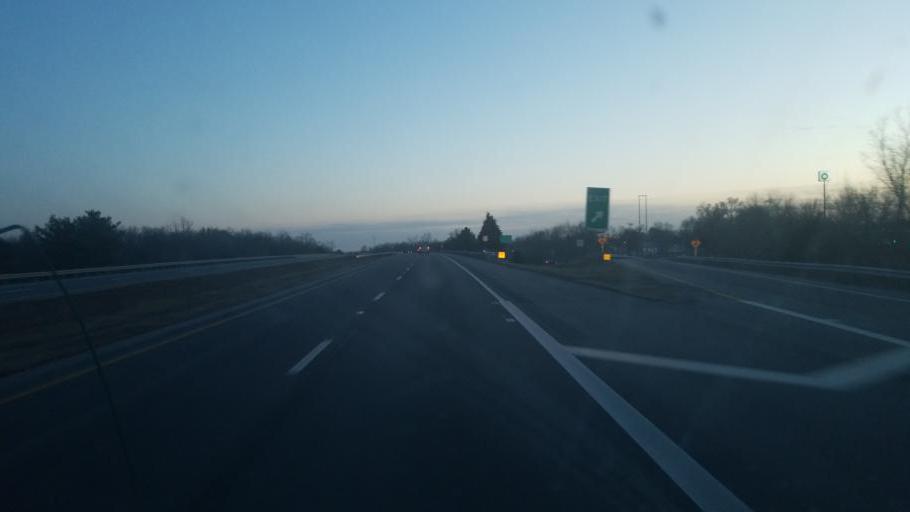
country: US
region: Ohio
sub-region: Marion County
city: Prospect
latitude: 40.4644
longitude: -83.0759
